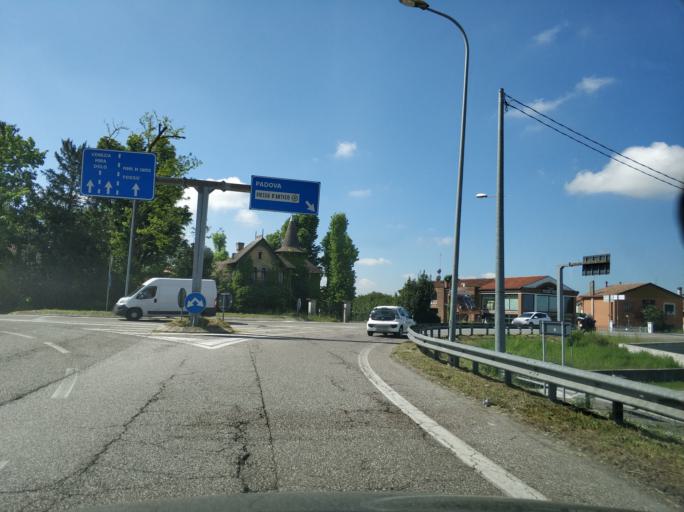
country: IT
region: Veneto
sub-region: Provincia di Venezia
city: Fiesso
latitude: 45.4186
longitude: 12.0517
